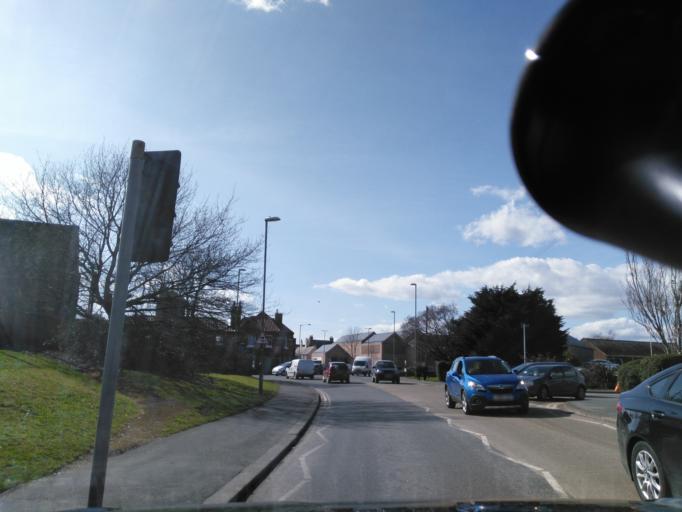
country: GB
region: England
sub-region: North Yorkshire
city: Northallerton
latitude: 54.3412
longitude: -1.4312
